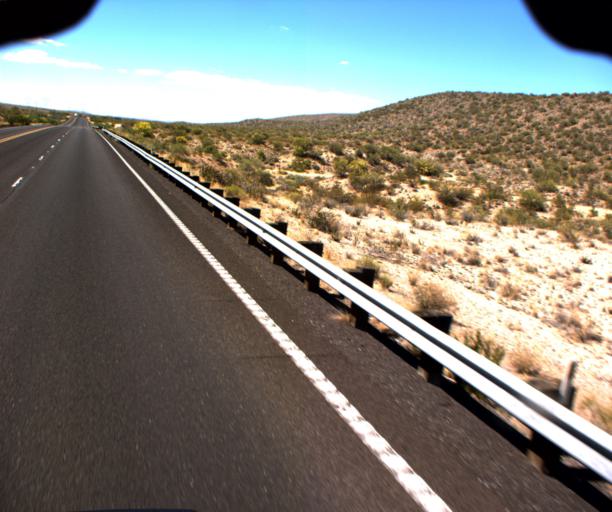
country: US
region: Arizona
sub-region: Mohave County
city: Kingman
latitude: 34.9346
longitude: -113.6615
